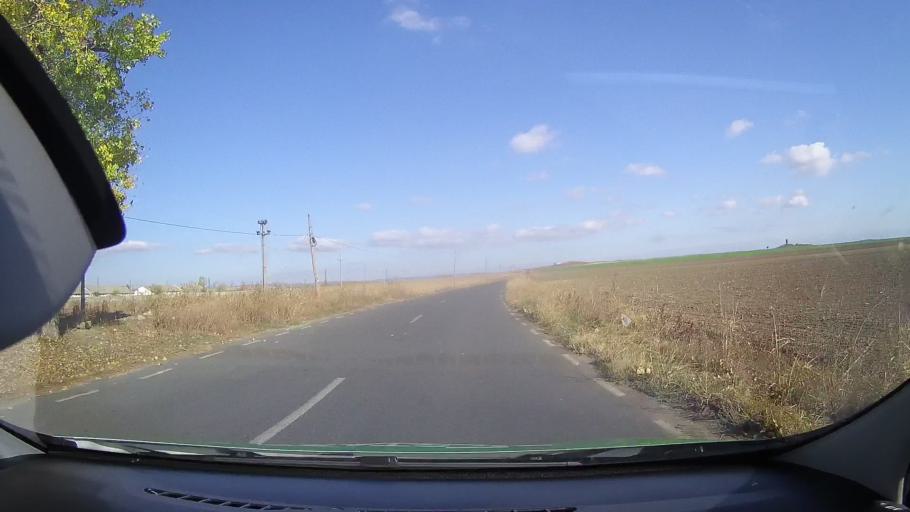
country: RO
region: Tulcea
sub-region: Comuna Ceamurlia de Jos
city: Ceamurlia de Jos
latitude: 44.7363
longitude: 28.6880
